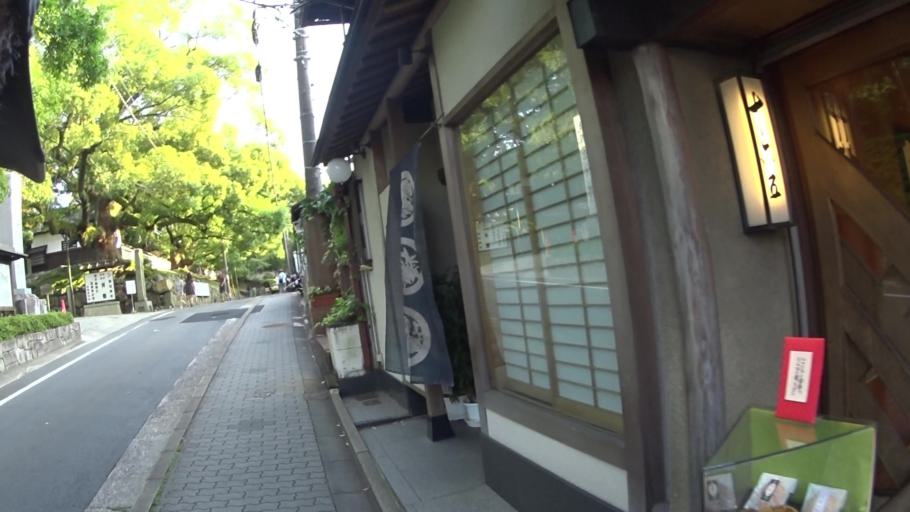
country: JP
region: Kyoto
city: Kyoto
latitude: 35.0082
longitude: 135.7827
